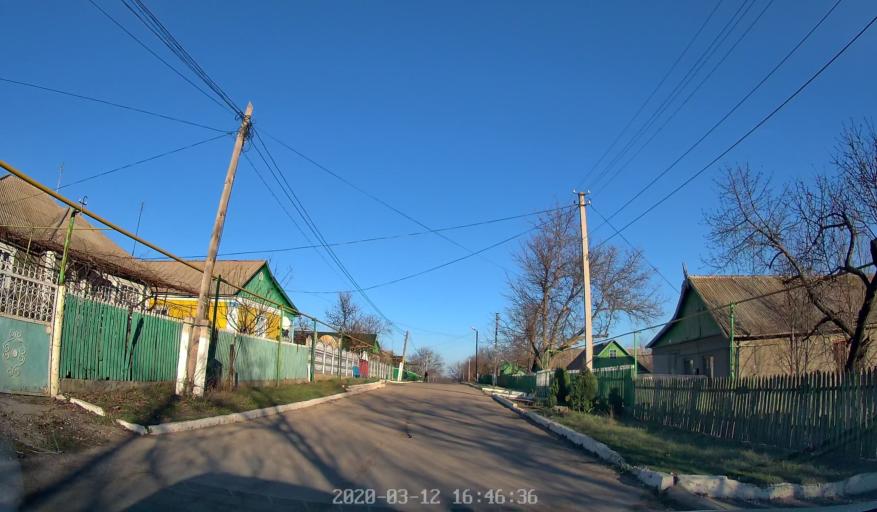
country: MD
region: Anenii Noi
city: Anenii Noi
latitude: 46.8141
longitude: 29.1798
